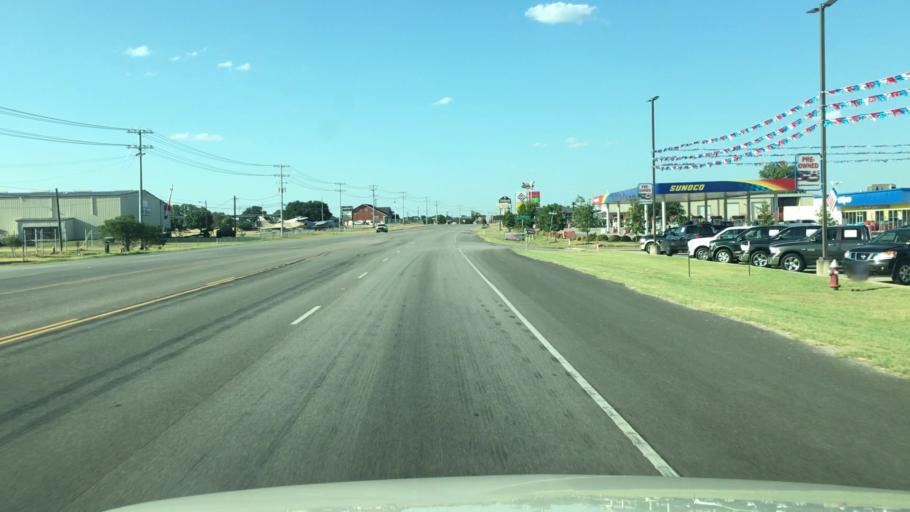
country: US
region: Texas
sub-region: Burnet County
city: Burnet
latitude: 30.7378
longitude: -98.2360
